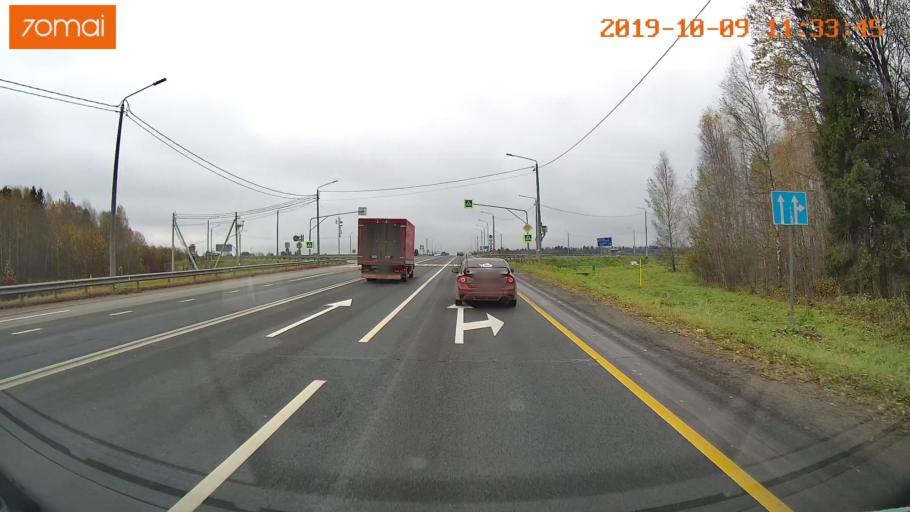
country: RU
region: Vologda
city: Gryazovets
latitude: 59.0220
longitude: 40.1152
